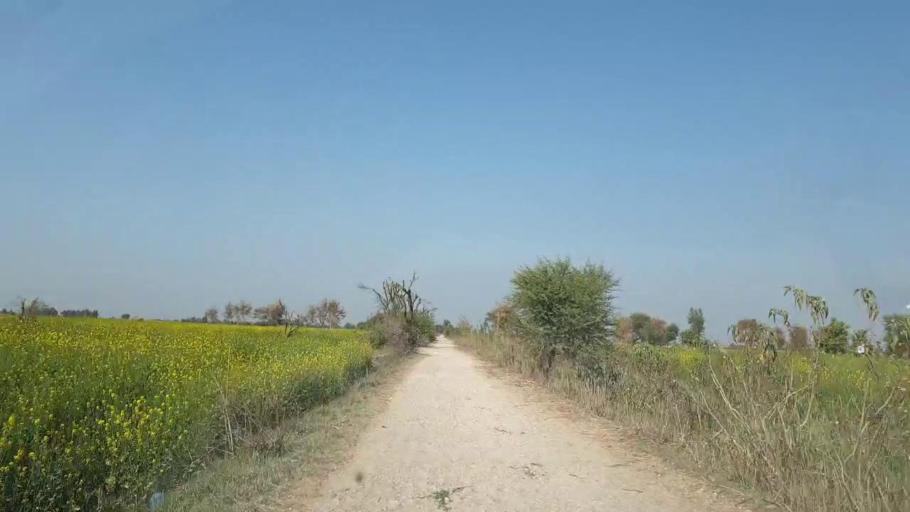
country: PK
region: Sindh
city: Mirpur Khas
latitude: 25.7239
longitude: 69.1393
